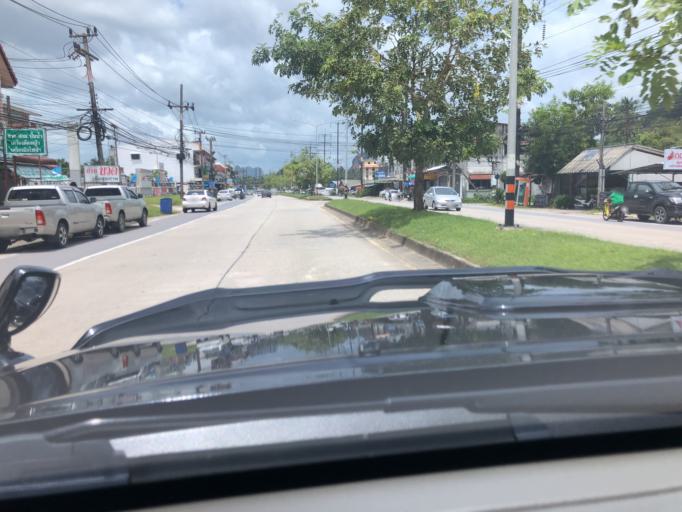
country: TH
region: Phangnga
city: Phang Nga
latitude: 8.4432
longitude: 98.5284
